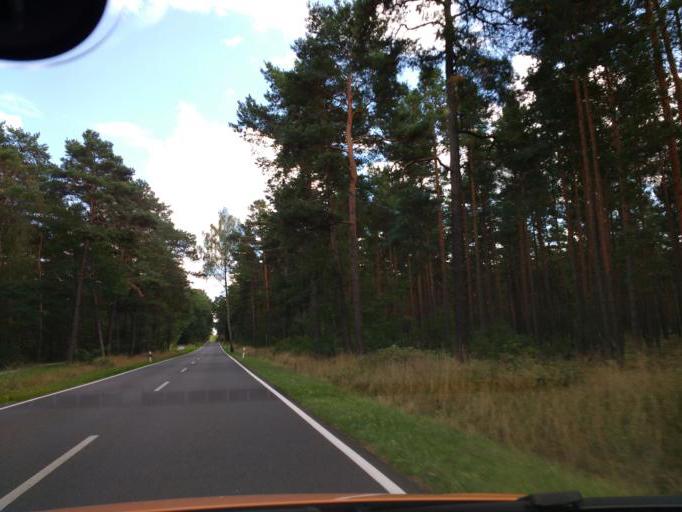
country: DE
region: Brandenburg
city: Wendisch Rietz
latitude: 52.2104
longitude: 13.9978
